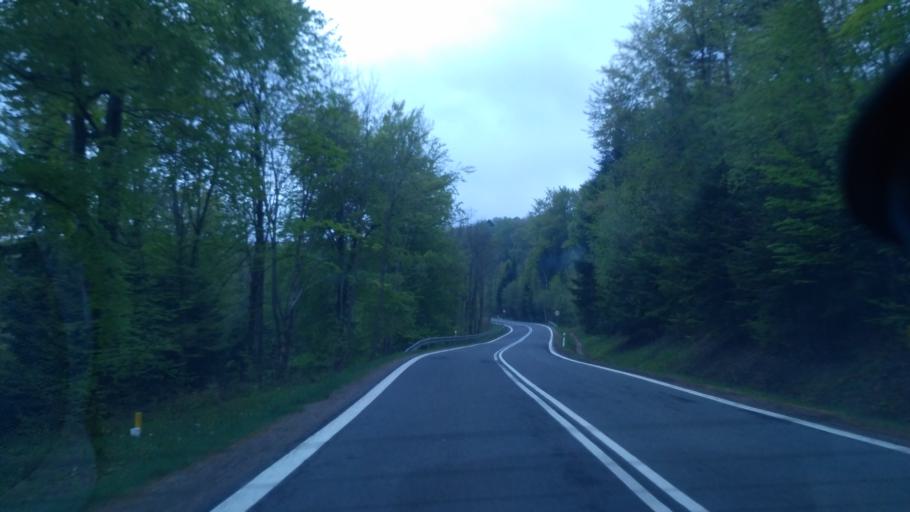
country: PL
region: Subcarpathian Voivodeship
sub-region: Powiat sanocki
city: Tyrawa Woloska
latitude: 49.5595
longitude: 22.3386
